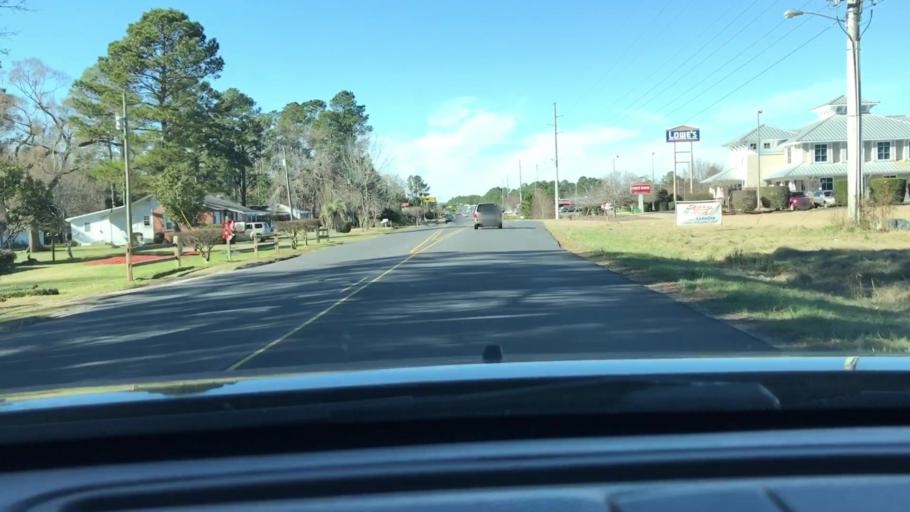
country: US
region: North Carolina
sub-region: Brunswick County
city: Shallotte
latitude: 33.9722
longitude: -78.3983
